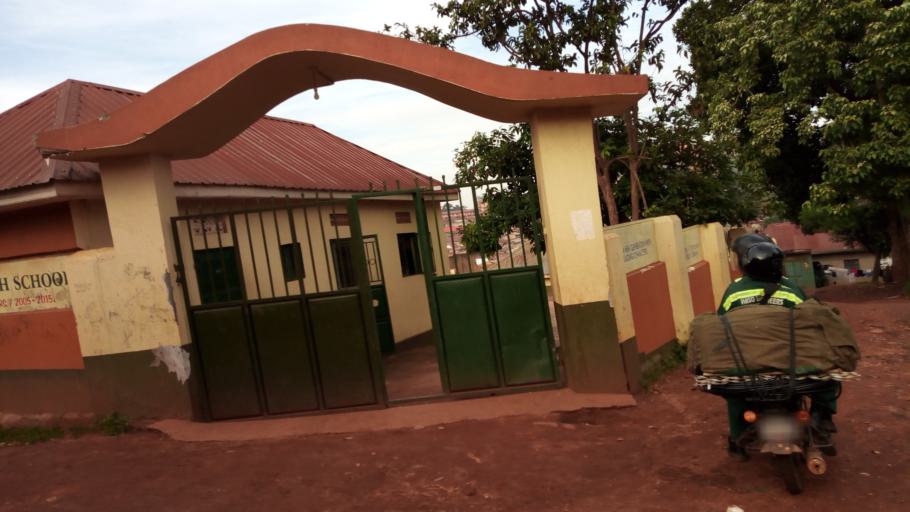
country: UG
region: Central Region
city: Kampala Central Division
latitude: 0.3723
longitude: 32.5539
